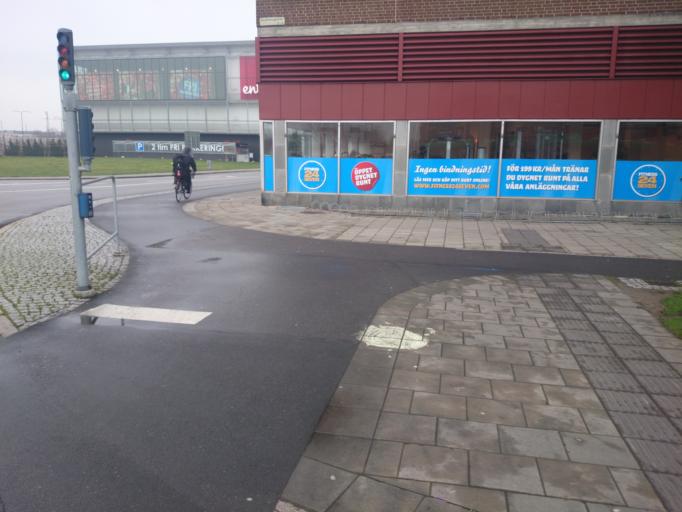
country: SE
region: Skane
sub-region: Malmo
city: Malmoe
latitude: 55.6079
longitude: 13.0214
